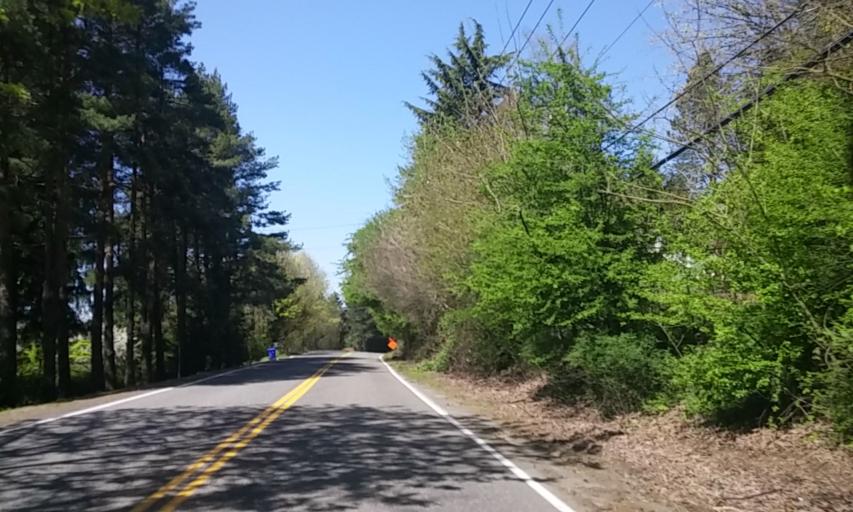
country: US
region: Oregon
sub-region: Washington County
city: West Haven
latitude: 45.5248
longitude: -122.7607
